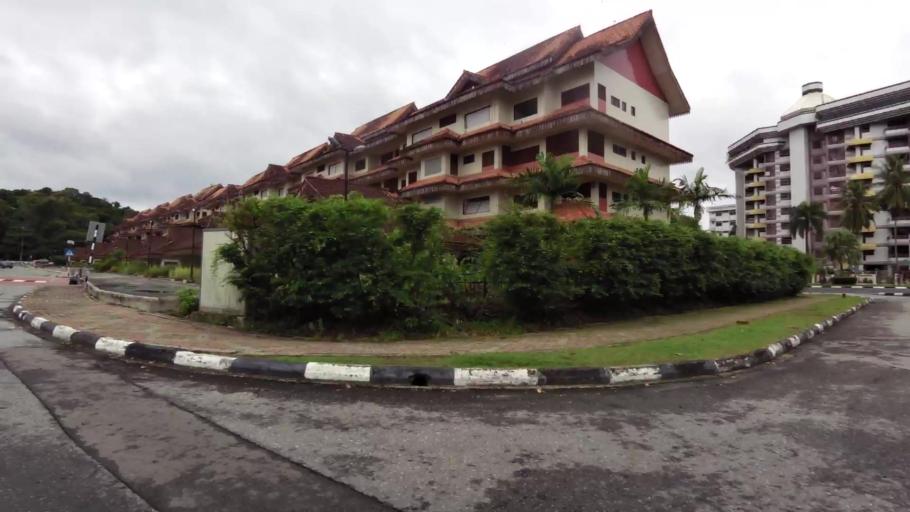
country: BN
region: Brunei and Muara
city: Bandar Seri Begawan
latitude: 4.8979
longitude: 114.9380
